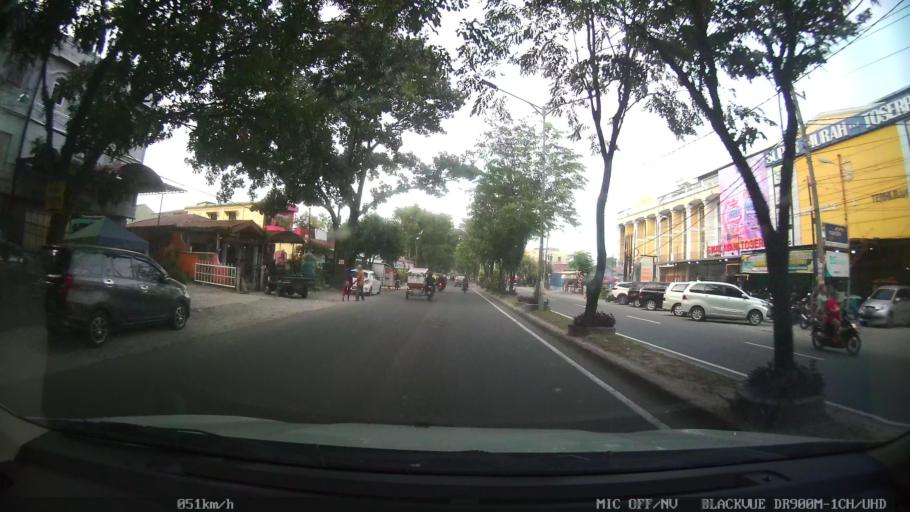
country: ID
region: North Sumatra
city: Sunggal
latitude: 3.5784
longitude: 98.6132
